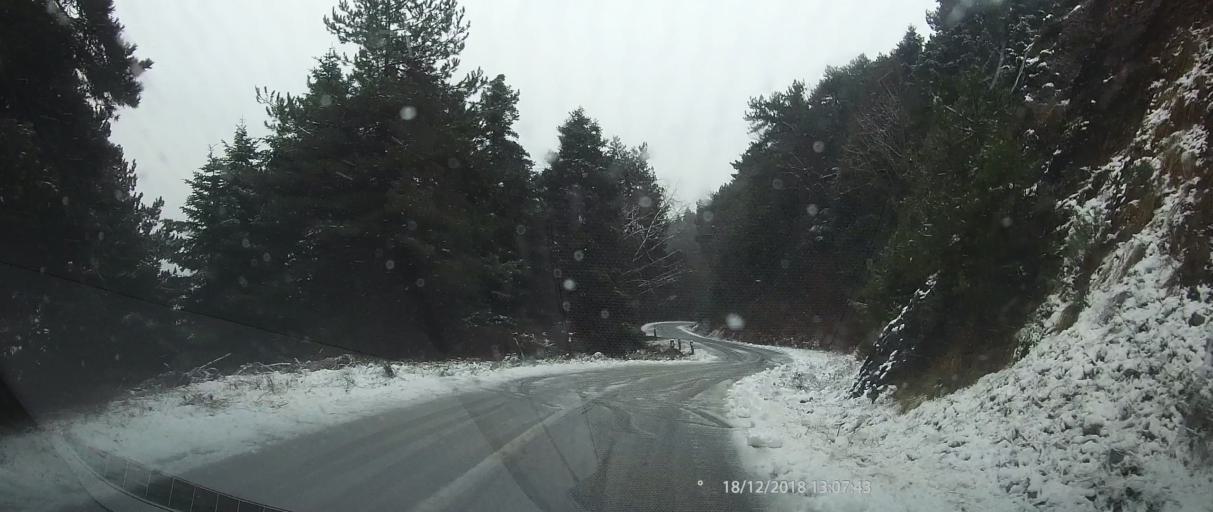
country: GR
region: Central Macedonia
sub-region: Nomos Pierias
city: Litochoro
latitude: 40.1074
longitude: 22.4745
